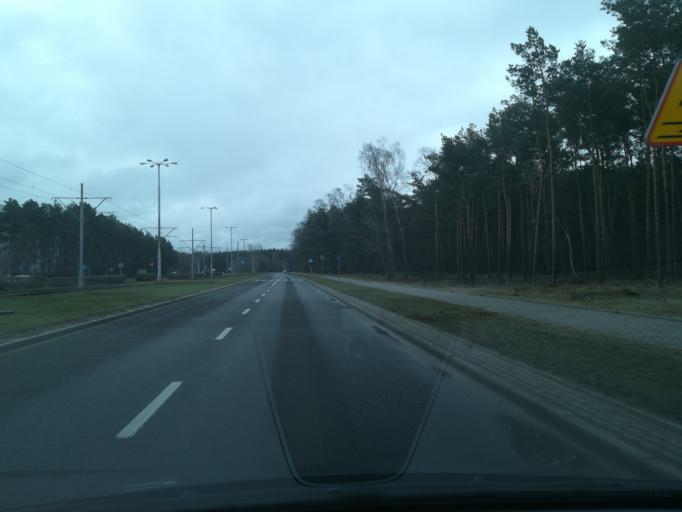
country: PL
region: Kujawsko-Pomorskie
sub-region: Powiat torunski
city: Lubicz Dolny
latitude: 53.0247
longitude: 18.6979
